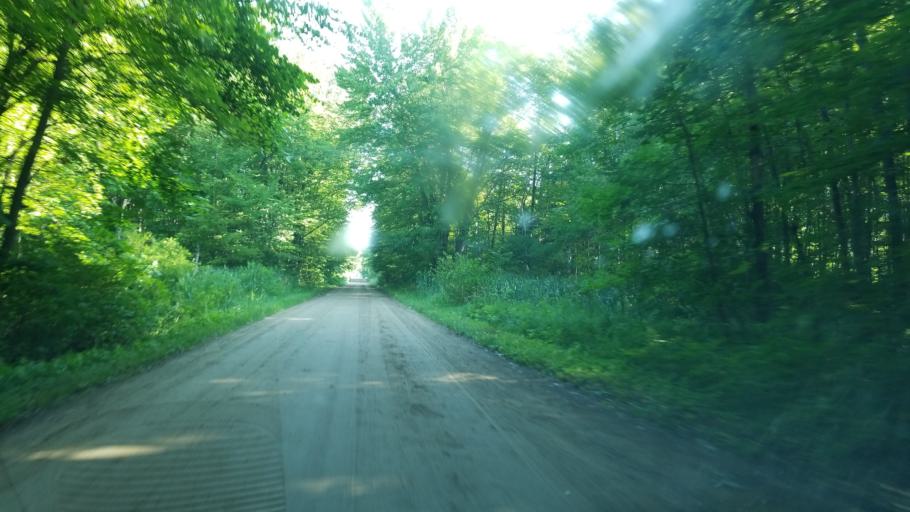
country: US
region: Michigan
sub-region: Mecosta County
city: Canadian Lakes
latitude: 43.5469
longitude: -85.4227
